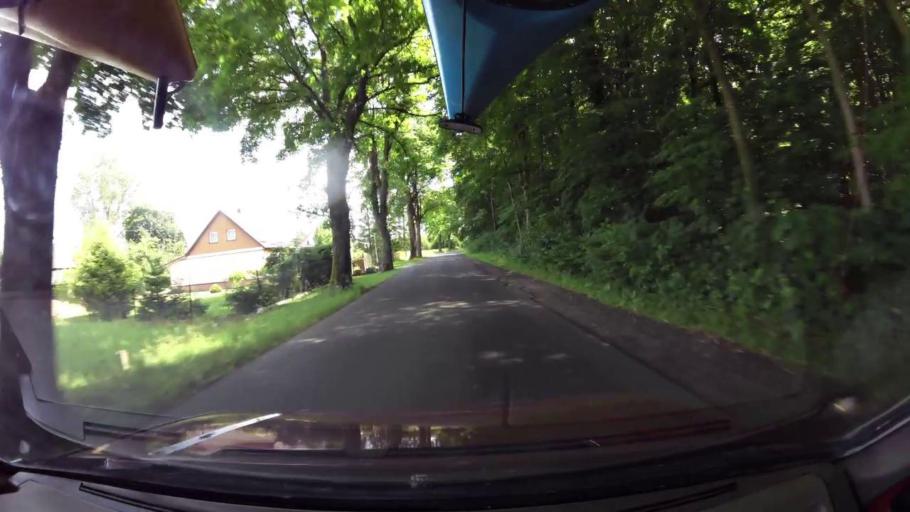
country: PL
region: West Pomeranian Voivodeship
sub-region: Powiat slawienski
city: Darlowo
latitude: 54.3263
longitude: 16.3737
